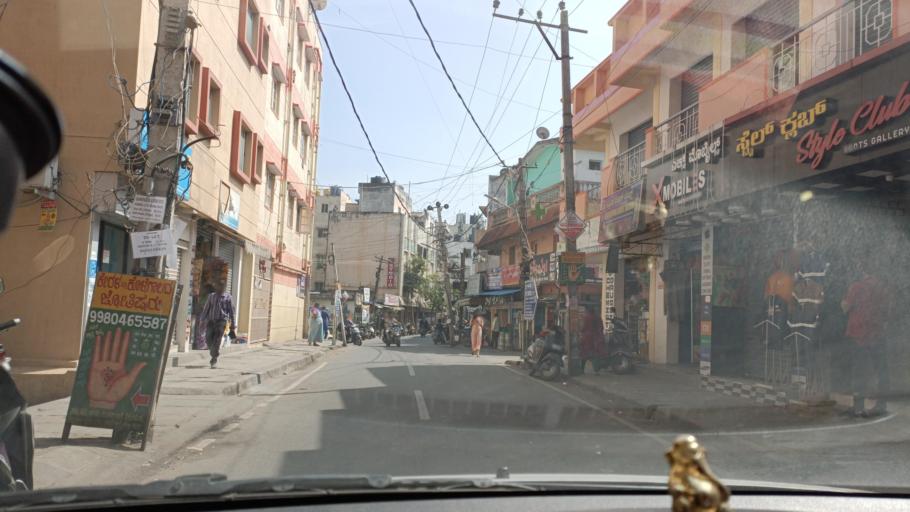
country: IN
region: Karnataka
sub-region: Bangalore Urban
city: Bangalore
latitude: 12.9200
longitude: 77.6170
